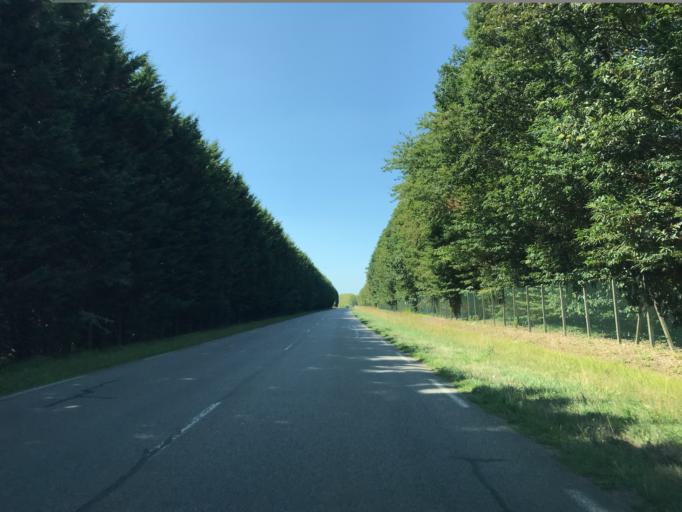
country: FR
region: Haute-Normandie
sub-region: Departement de l'Eure
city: Saint-Just
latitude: 49.0940
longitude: 1.4193
